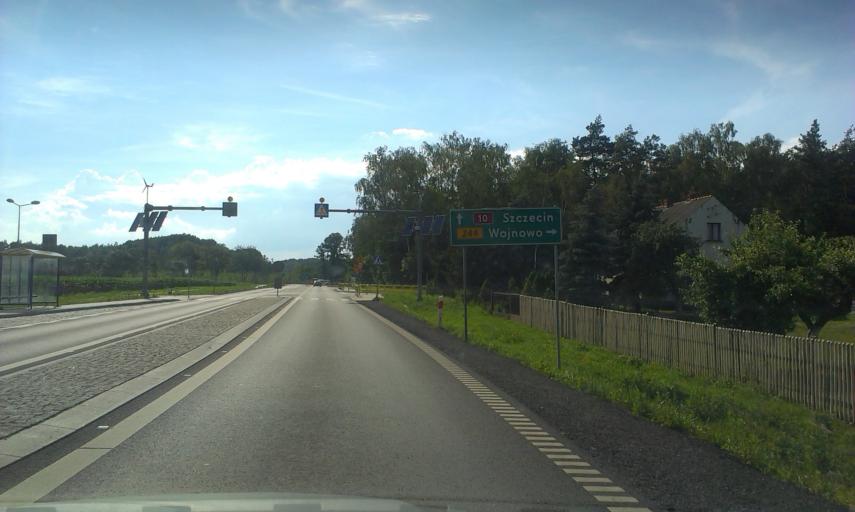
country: PL
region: Kujawsko-Pomorskie
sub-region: Powiat bydgoski
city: Sicienko
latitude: 53.1609
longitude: 17.8156
